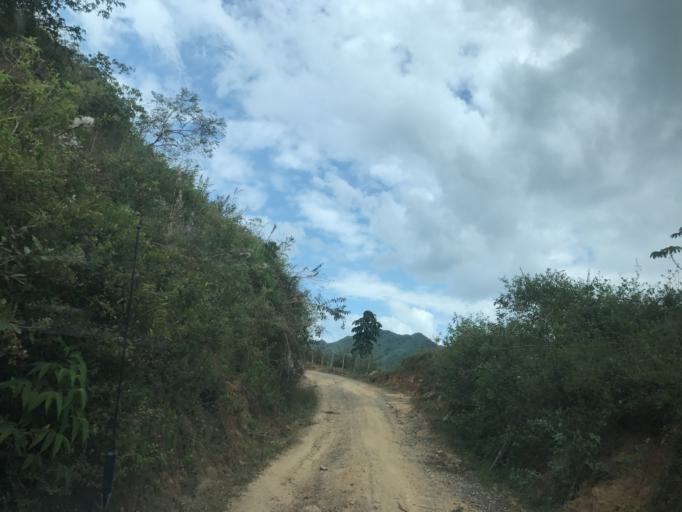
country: CO
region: Valle del Cauca
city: Obando
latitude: 4.5527
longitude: -75.9171
